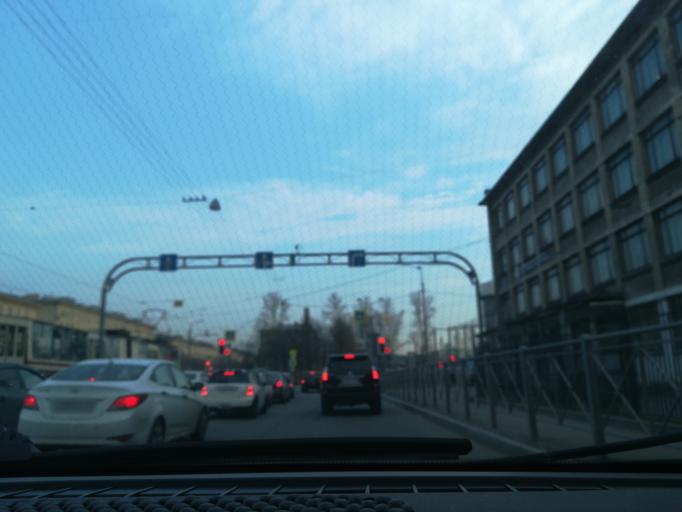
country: RU
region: St.-Petersburg
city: Avtovo
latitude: 59.8734
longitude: 30.2544
